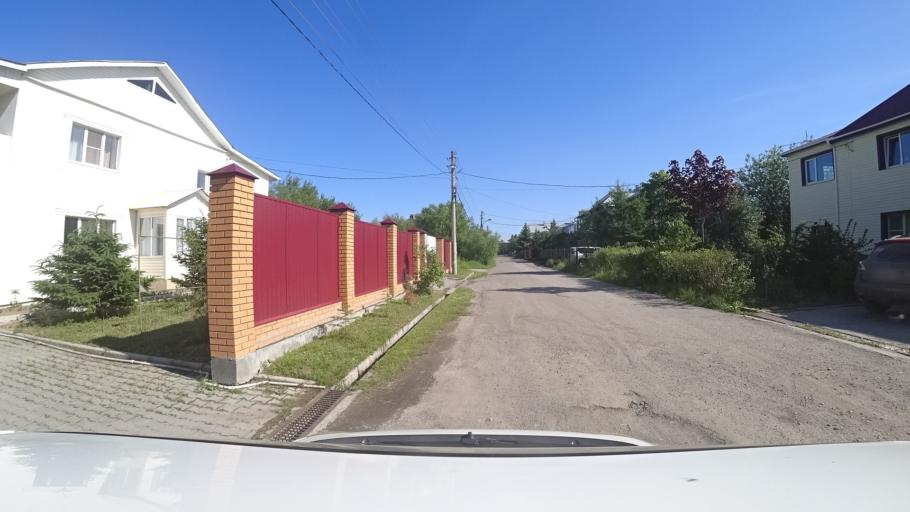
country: RU
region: Khabarovsk Krai
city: Topolevo
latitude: 48.5433
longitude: 135.1763
